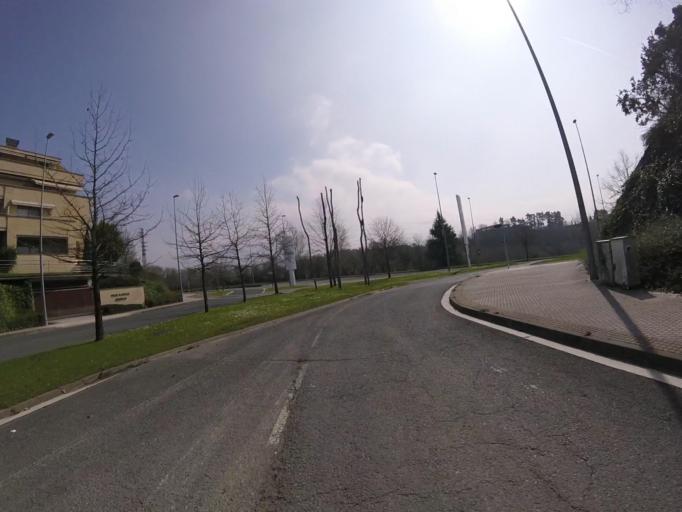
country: ES
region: Basque Country
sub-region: Provincia de Guipuzcoa
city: Hernani
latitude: 43.2871
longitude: -1.9825
